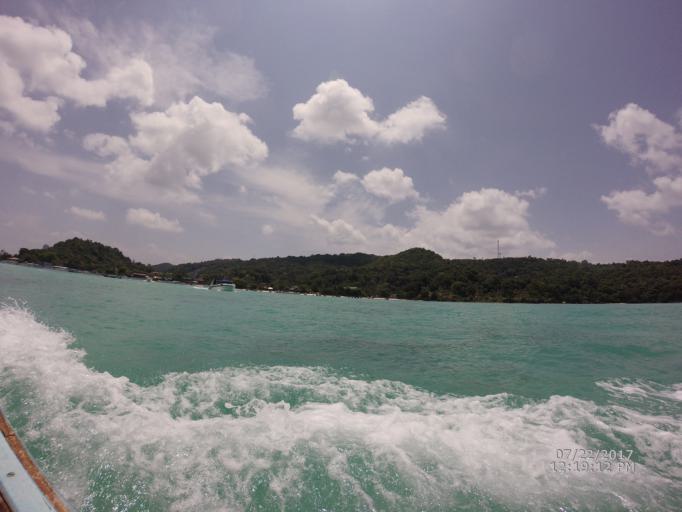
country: TH
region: Krabi
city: Saladan
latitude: 7.7323
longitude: 98.7775
